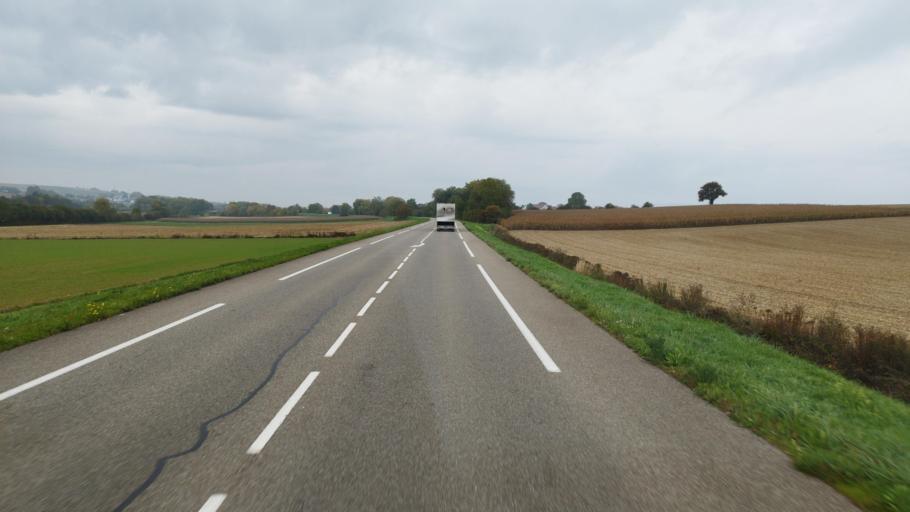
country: FR
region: Alsace
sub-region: Departement du Bas-Rhin
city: Betschdorf
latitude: 48.9326
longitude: 7.9261
